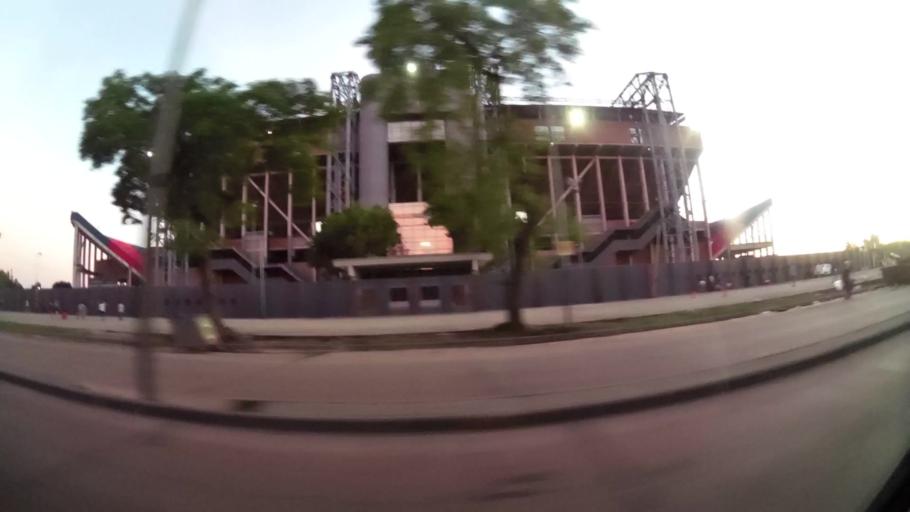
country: AR
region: Buenos Aires F.D.
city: Villa Lugano
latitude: -34.6510
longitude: -58.4406
